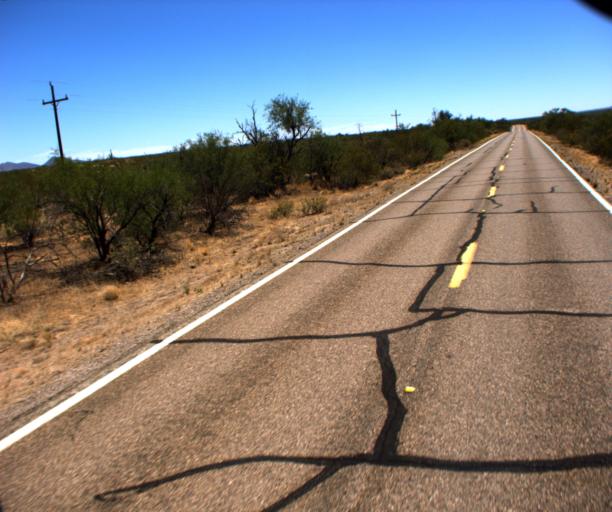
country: US
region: Arizona
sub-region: Pima County
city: Three Points
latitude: 31.9625
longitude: -111.3857
